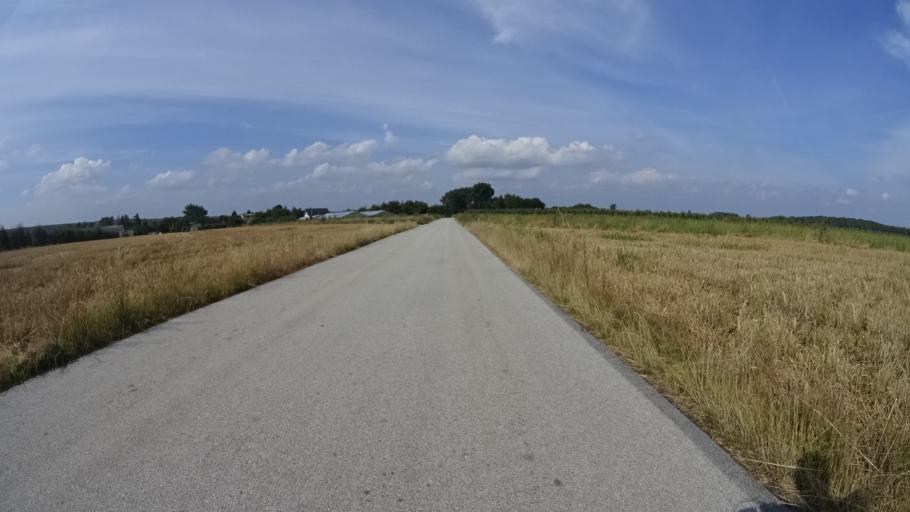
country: PL
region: Masovian Voivodeship
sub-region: Powiat grojecki
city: Goszczyn
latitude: 51.6950
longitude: 20.8474
